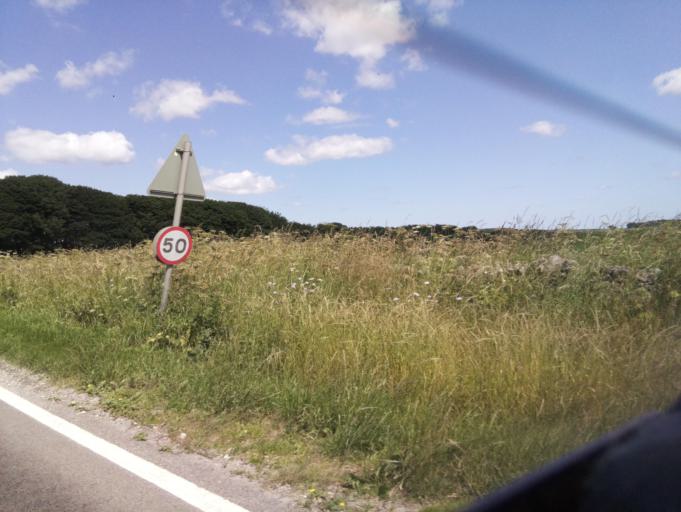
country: GB
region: England
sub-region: Derbyshire
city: Bakewell
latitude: 53.1550
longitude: -1.7706
